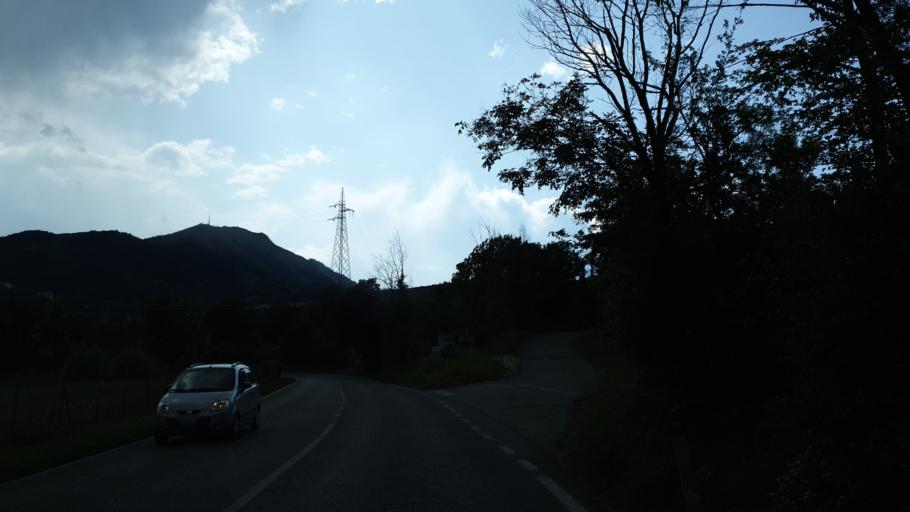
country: IT
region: Emilia-Romagna
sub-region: Provincia di Rimini
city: Talamello
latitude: 43.9106
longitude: 12.3001
